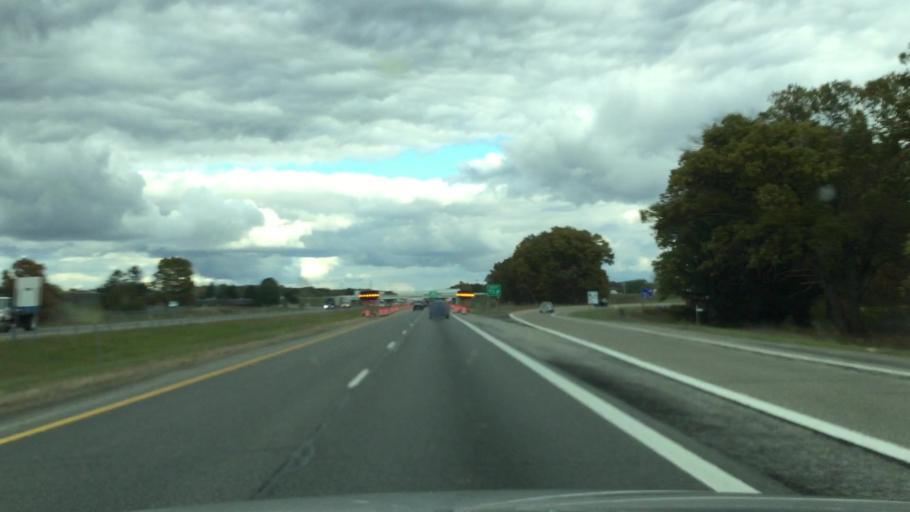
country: US
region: Michigan
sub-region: Kalamazoo County
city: Westwood
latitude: 42.2376
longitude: -85.6854
